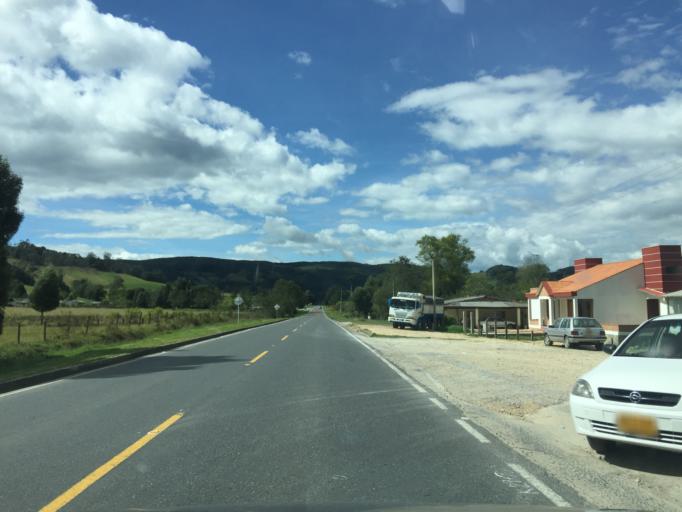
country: CO
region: Boyaca
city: Arcabuco
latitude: 5.7810
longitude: -73.4610
